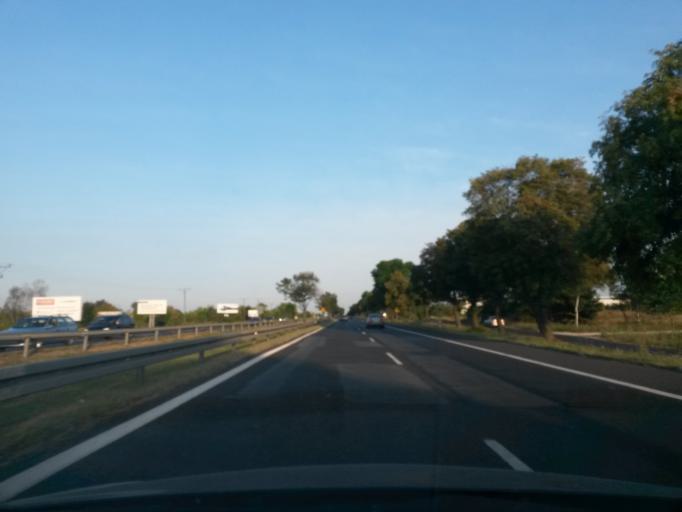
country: PL
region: Masovian Voivodeship
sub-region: Powiat nowodworski
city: Nowy Dwor Mazowiecki
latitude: 52.3811
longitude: 20.7617
